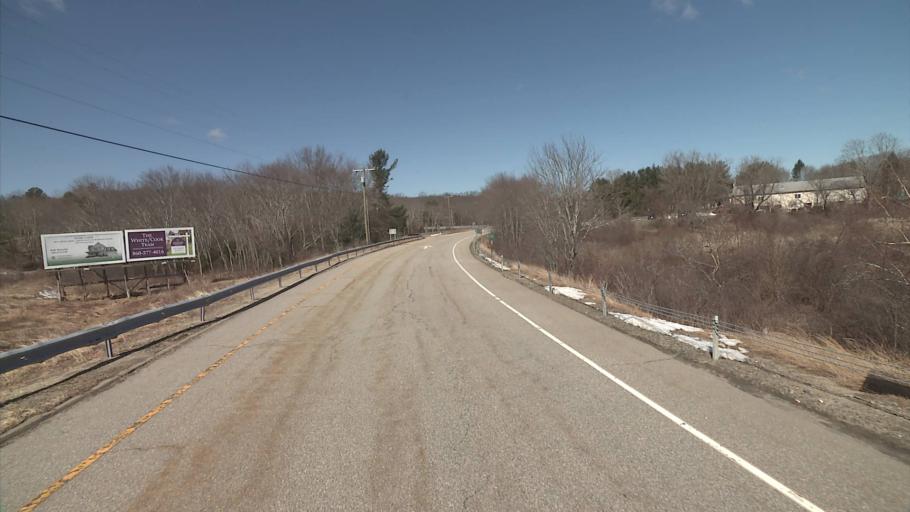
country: US
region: Connecticut
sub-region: Windham County
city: Danielson
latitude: 41.7897
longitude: -71.8448
